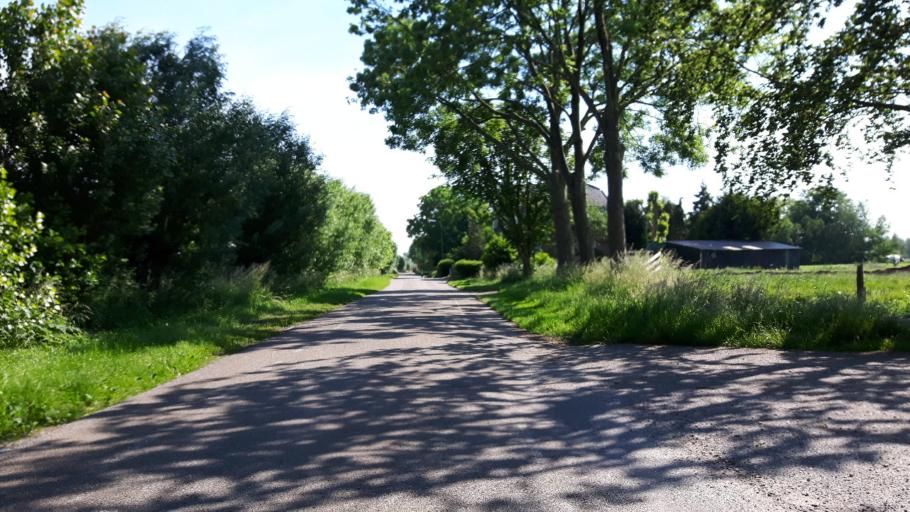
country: NL
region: Utrecht
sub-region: Stichtse Vecht
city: Breukelen
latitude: 52.2013
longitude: 4.9751
